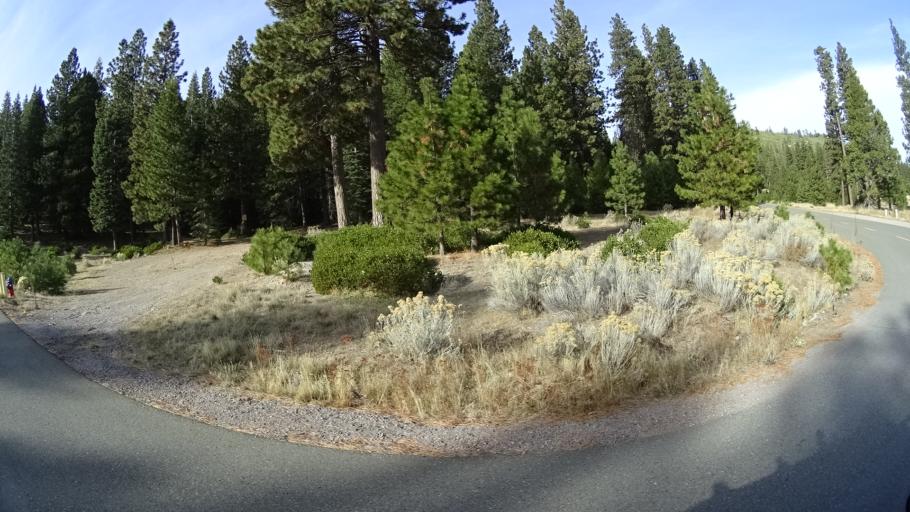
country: US
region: California
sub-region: Siskiyou County
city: Weed
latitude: 41.3976
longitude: -122.3896
